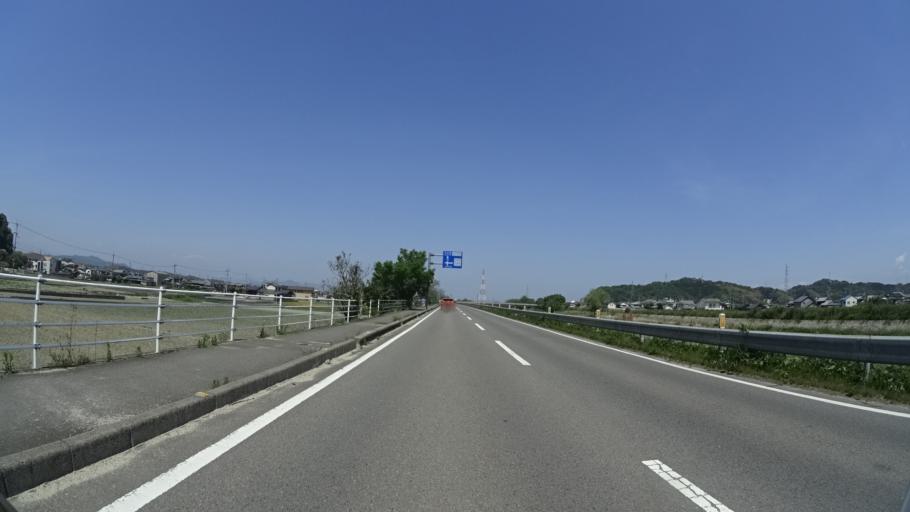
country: JP
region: Ehime
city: Hojo
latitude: 34.0306
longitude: 132.9657
